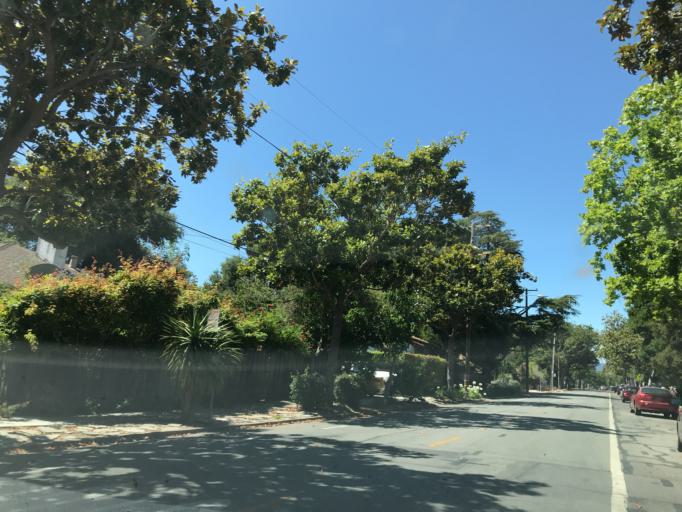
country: US
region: California
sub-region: Santa Clara County
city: Palo Alto
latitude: 37.4481
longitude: -122.1495
